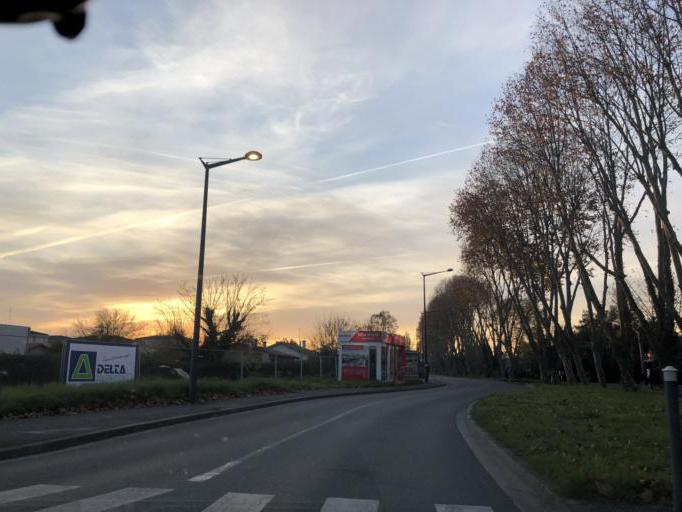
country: FR
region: Aquitaine
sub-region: Departement de la Gironde
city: Le Bouscat
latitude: 44.8851
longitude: -0.5875
